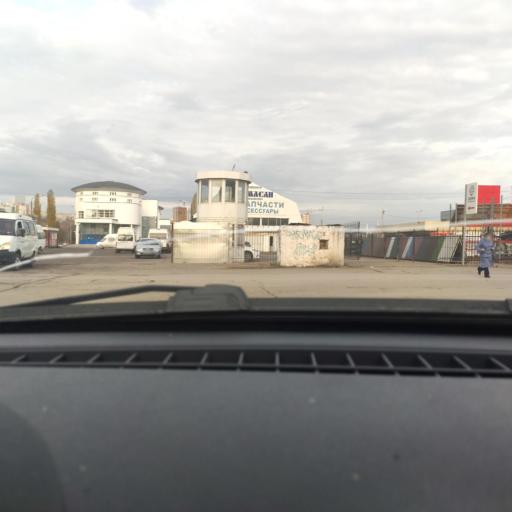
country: RU
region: Bashkortostan
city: Ufa
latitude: 54.7722
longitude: 56.0652
